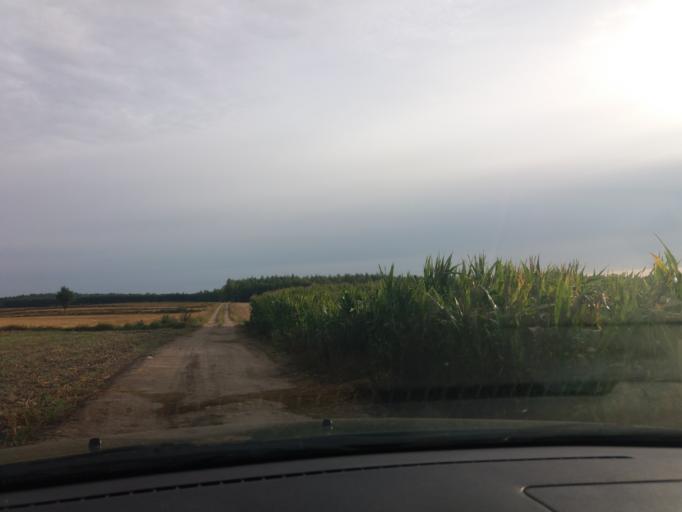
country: PL
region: Masovian Voivodeship
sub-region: Powiat mlawski
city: Wieczfnia Koscielna
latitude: 53.2130
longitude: 20.4549
